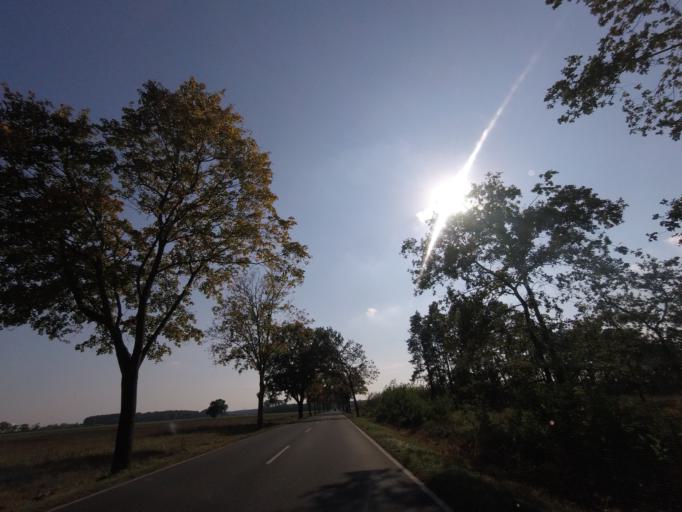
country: DE
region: Saxony-Anhalt
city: Jessen
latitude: 51.8294
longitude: 13.0167
